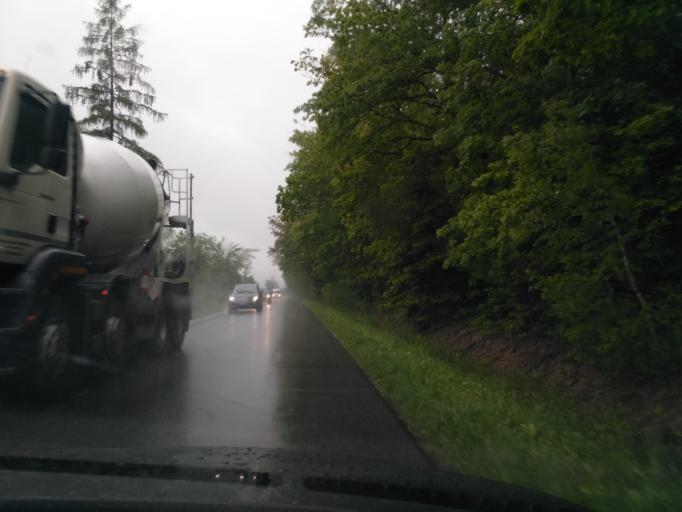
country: PL
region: Subcarpathian Voivodeship
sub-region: Powiat jasielski
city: Debowiec
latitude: 49.6558
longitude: 21.4174
